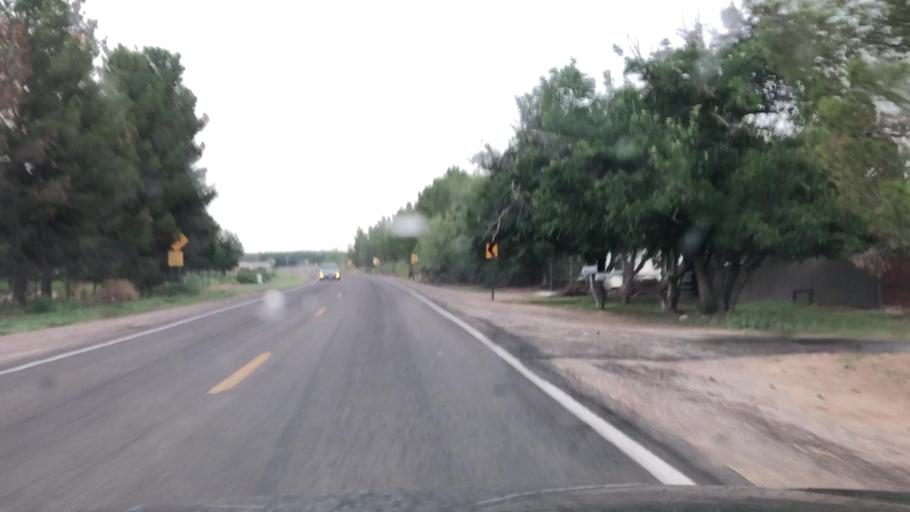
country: US
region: New Mexico
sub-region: Dona Ana County
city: Vado
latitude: 32.1120
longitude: -106.6720
